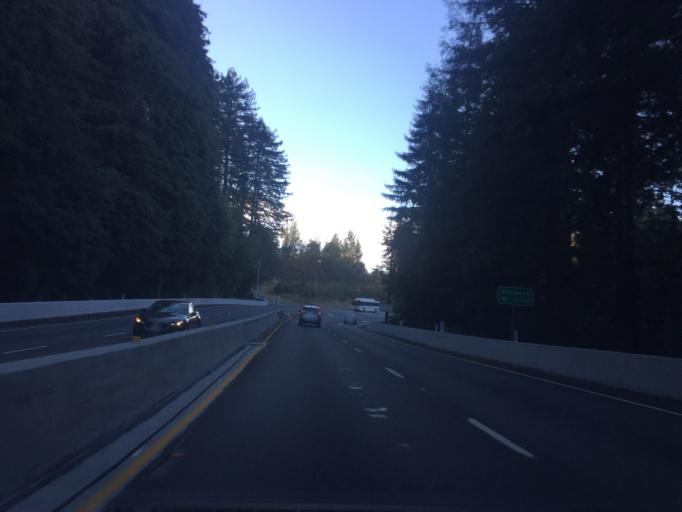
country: US
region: California
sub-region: Santa Clara County
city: Lexington Hills
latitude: 37.1188
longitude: -121.9752
